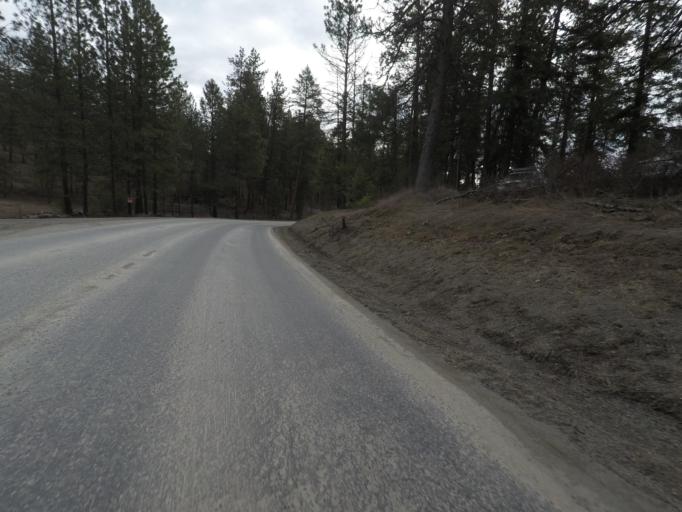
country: US
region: Washington
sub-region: Stevens County
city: Colville
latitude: 48.5038
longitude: -117.8529
